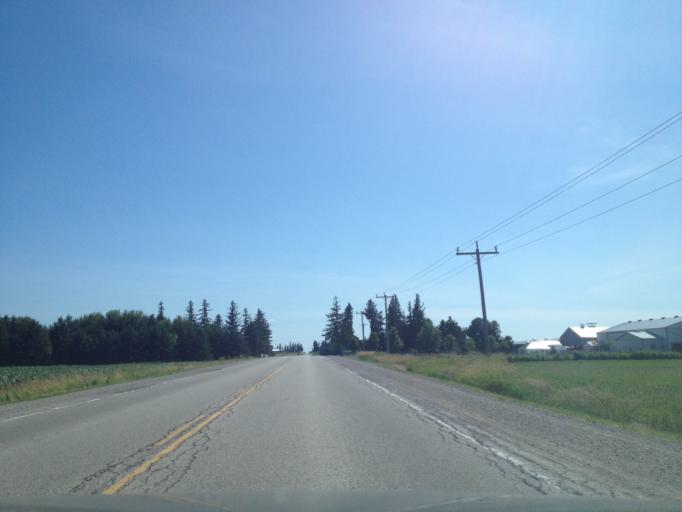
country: CA
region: Ontario
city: Waterloo
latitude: 43.5209
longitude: -80.7493
